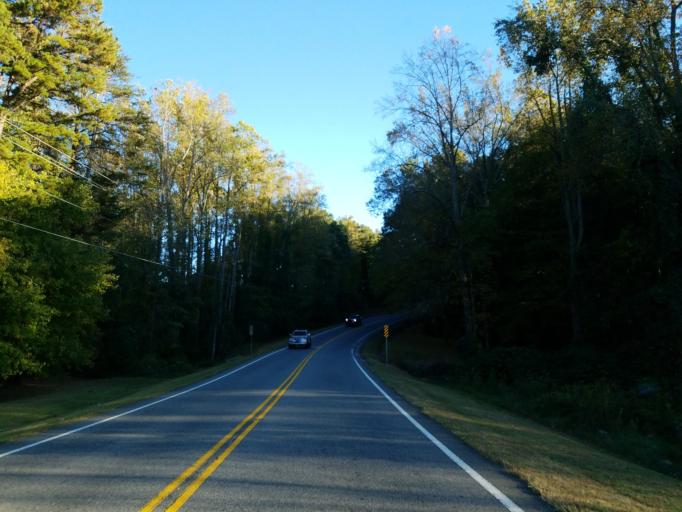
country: US
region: Georgia
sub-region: Dawson County
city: Dawsonville
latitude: 34.4145
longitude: -84.1178
